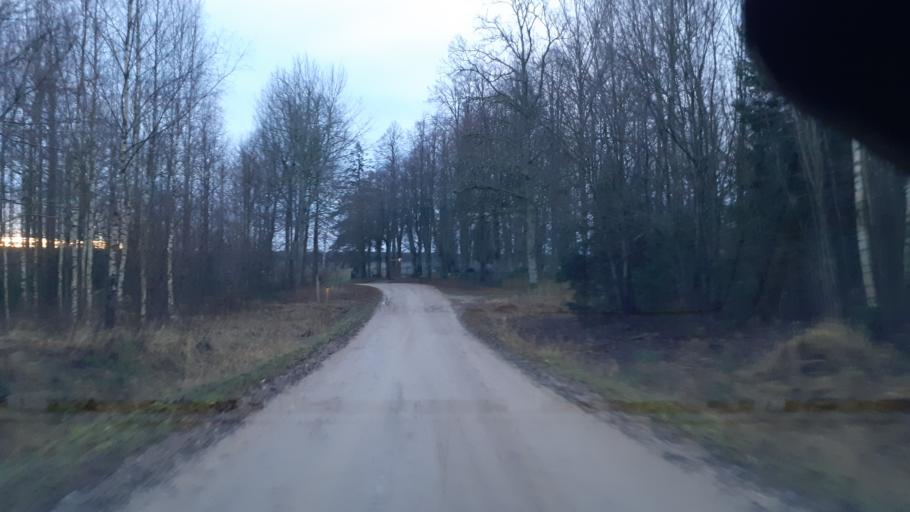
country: LV
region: Alsunga
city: Alsunga
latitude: 56.9082
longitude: 21.7126
